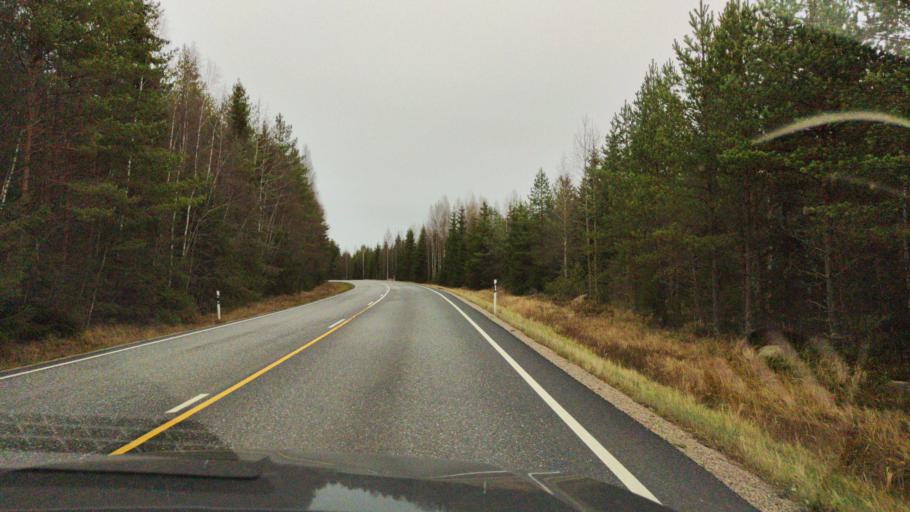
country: FI
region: Varsinais-Suomi
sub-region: Loimaa
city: Aura
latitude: 60.7215
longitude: 22.4451
